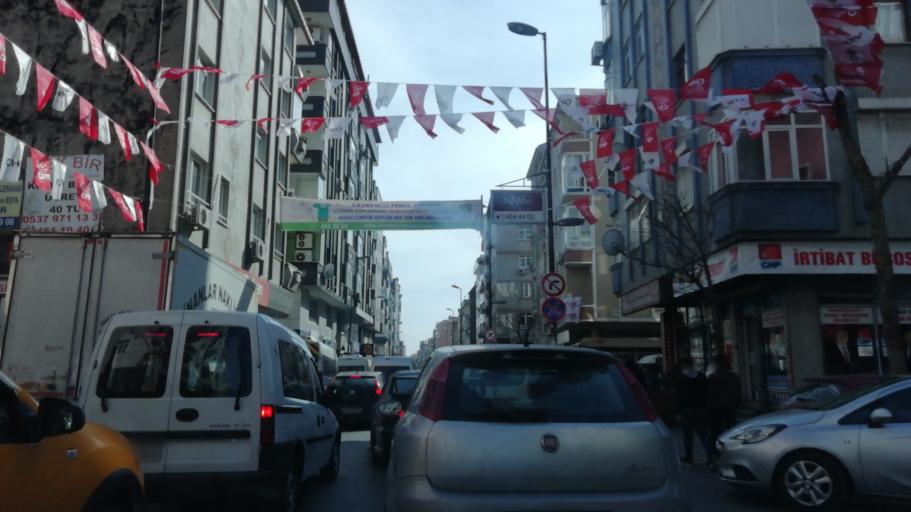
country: TR
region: Istanbul
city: Bahcelievler
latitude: 40.9985
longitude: 28.8386
